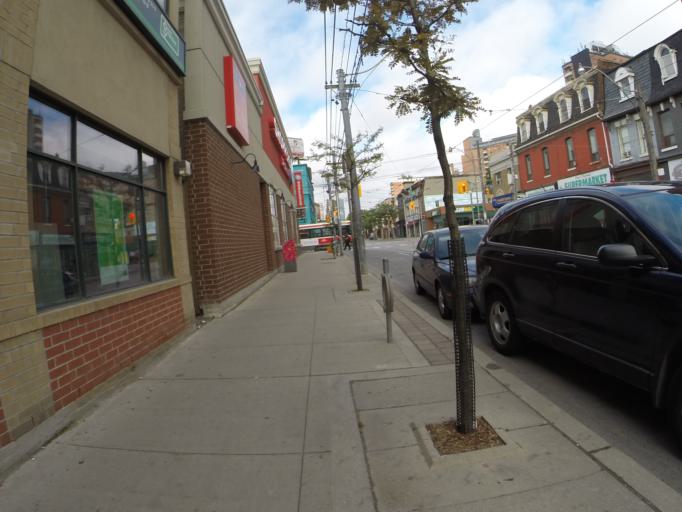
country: CA
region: Ontario
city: Toronto
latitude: 43.6562
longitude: -79.3622
